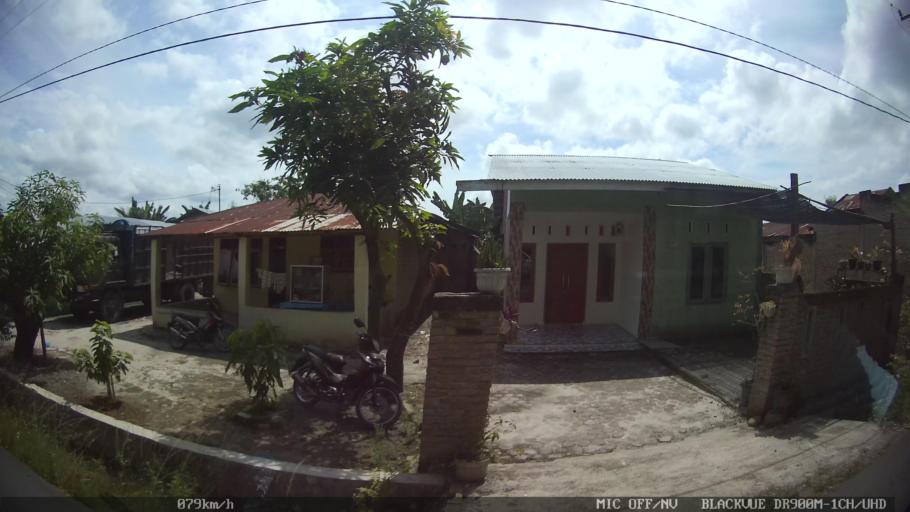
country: ID
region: North Sumatra
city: Percut
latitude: 3.5937
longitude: 98.8605
